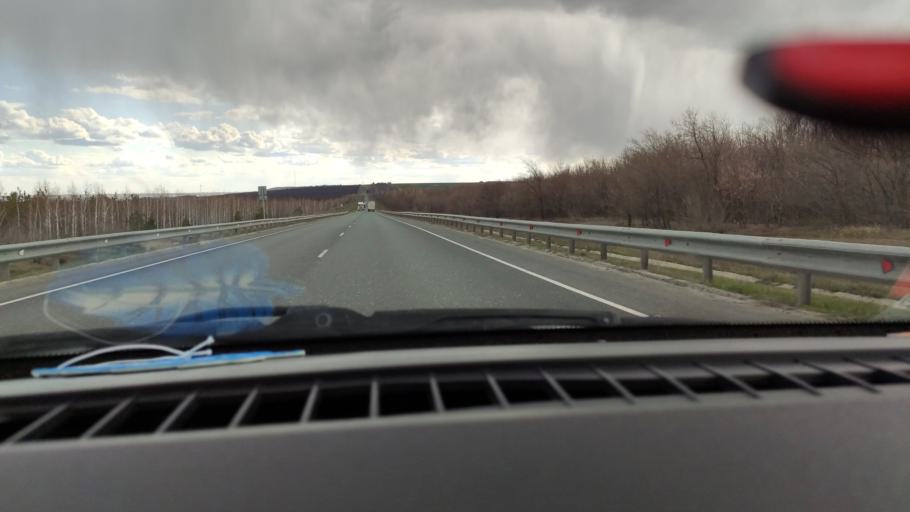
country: RU
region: Saratov
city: Balakovo
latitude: 52.1500
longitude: 47.8111
